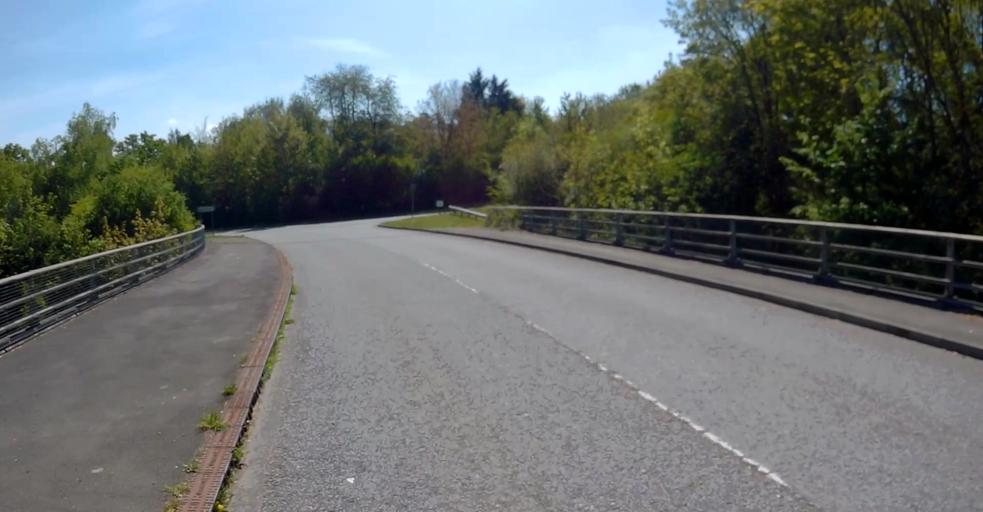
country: GB
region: England
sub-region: Hampshire
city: Andover
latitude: 51.1875
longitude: -1.4095
